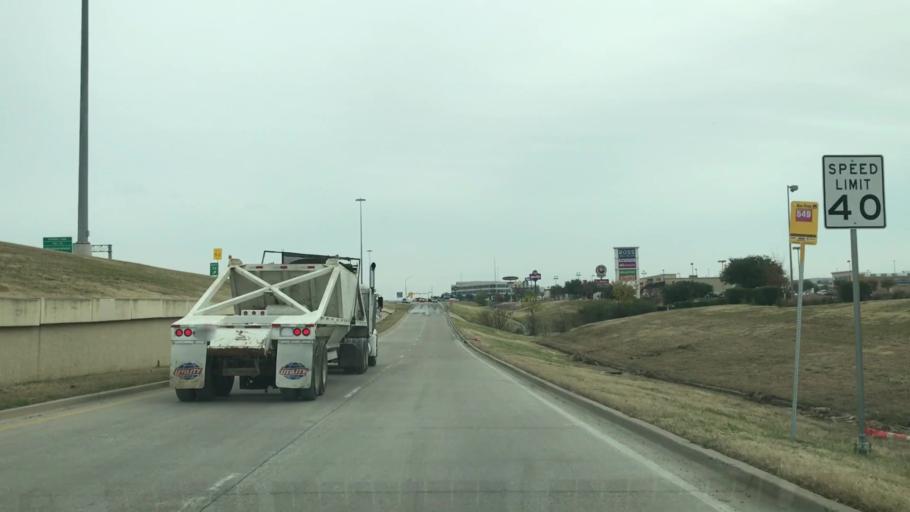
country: US
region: Texas
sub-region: Dallas County
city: Cockrell Hill
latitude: 32.7659
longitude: -96.9018
